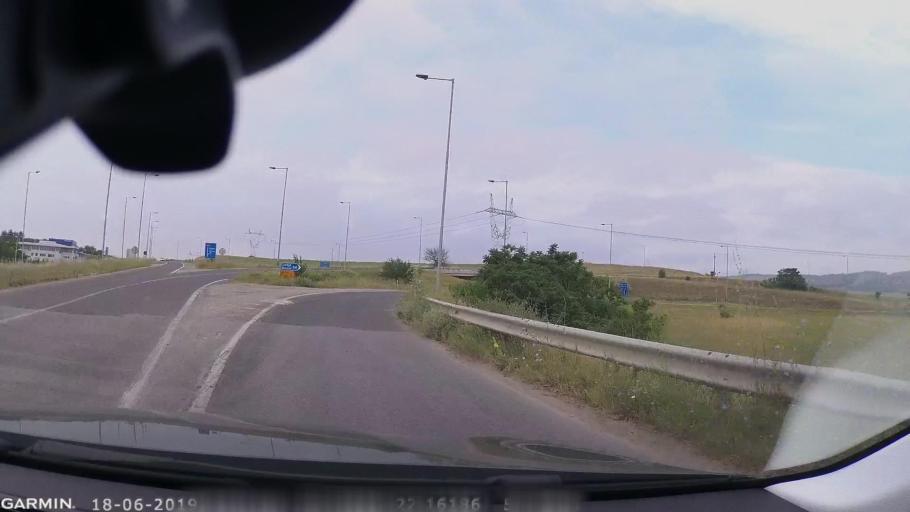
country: MK
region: Stip
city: Shtip
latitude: 41.7636
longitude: 22.1616
